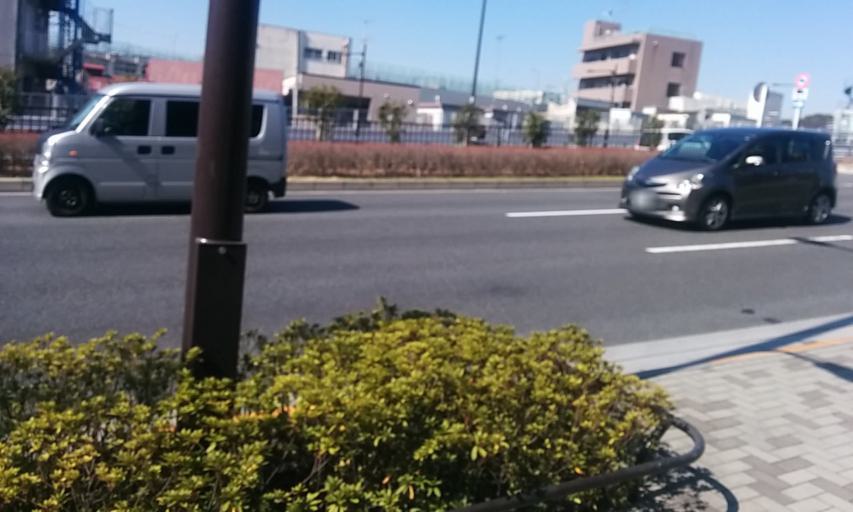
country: JP
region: Tokyo
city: Tokyo
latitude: 35.6688
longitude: 139.6881
